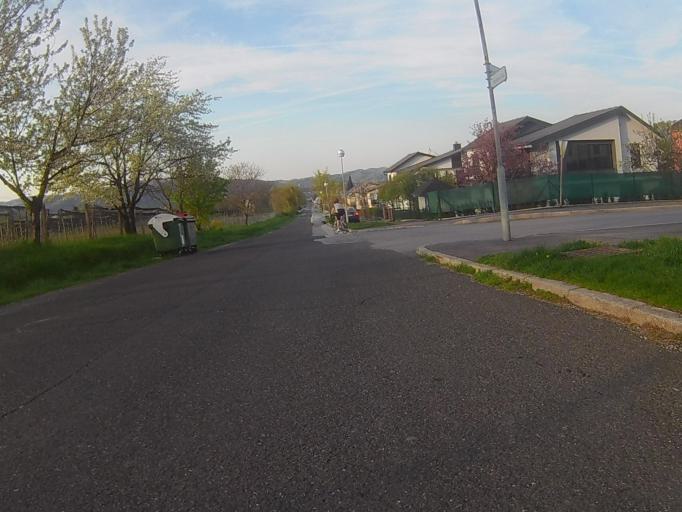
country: SI
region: Maribor
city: Pekre
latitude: 46.5386
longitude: 15.5882
